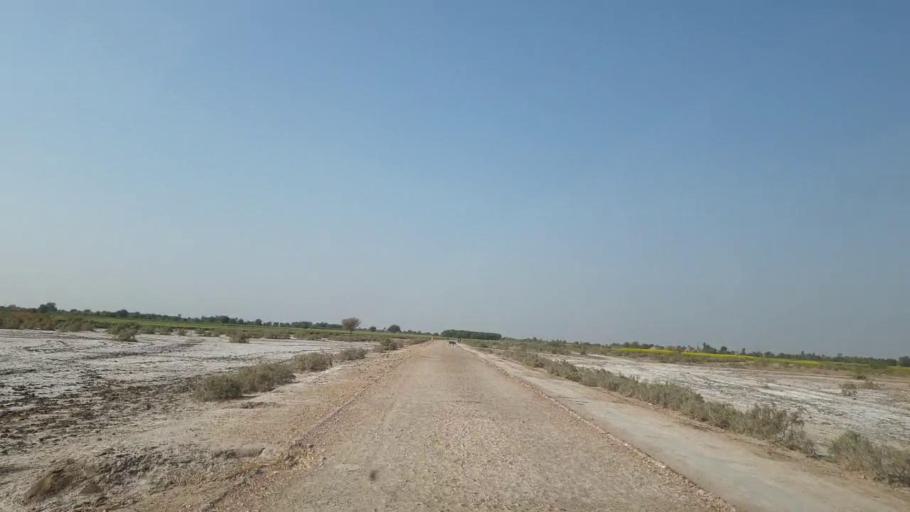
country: PK
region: Sindh
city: Tando Mittha Khan
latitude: 25.7580
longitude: 69.1949
